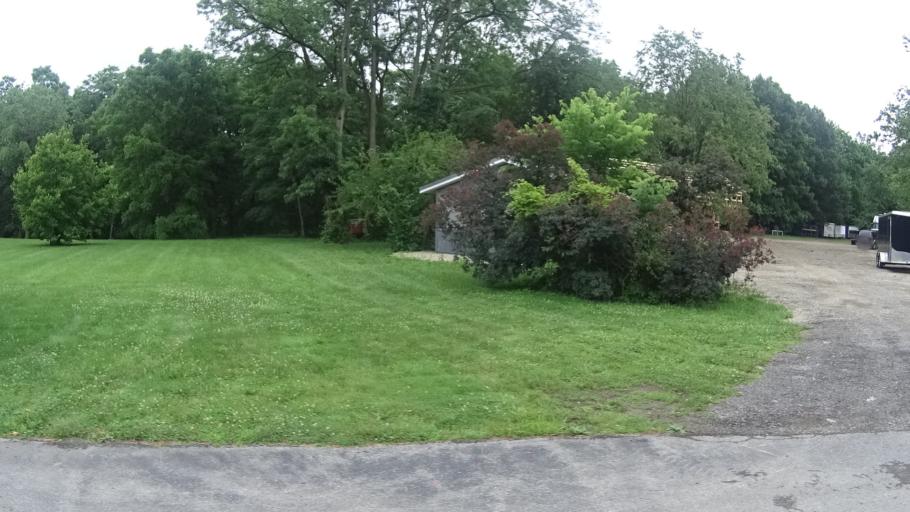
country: US
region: Ohio
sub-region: Erie County
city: Huron
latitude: 41.3277
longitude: -82.4871
